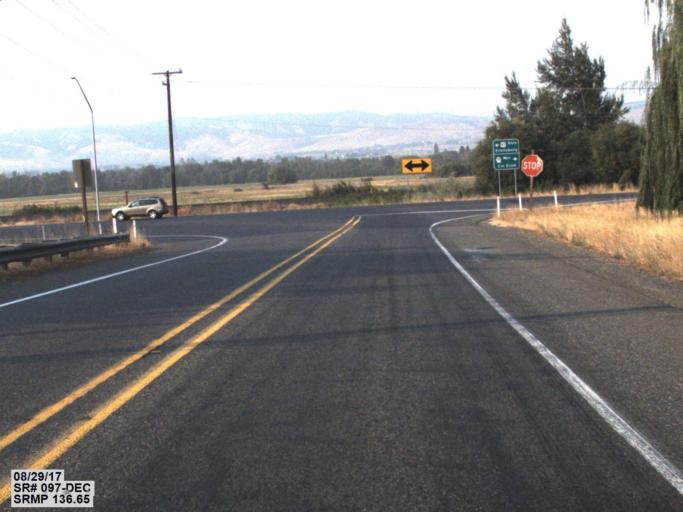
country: US
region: Washington
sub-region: Kittitas County
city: Ellensburg
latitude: 47.0350
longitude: -120.6101
